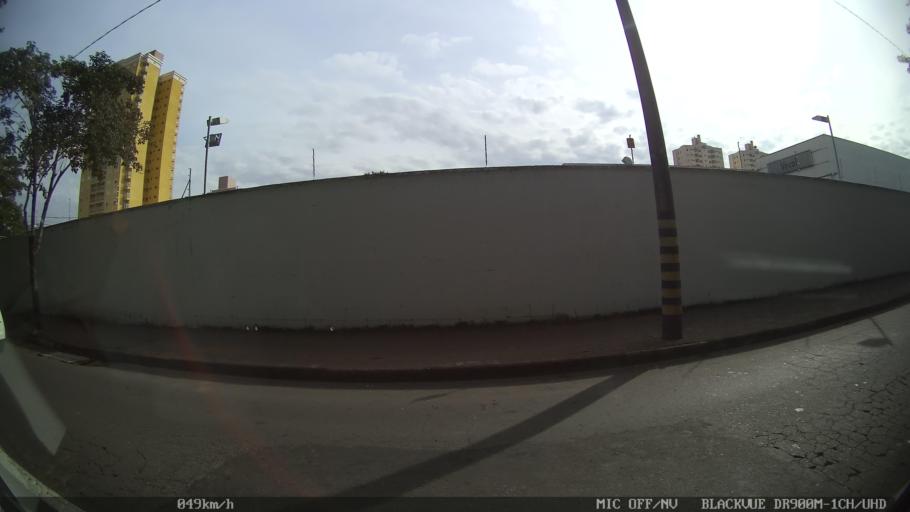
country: BR
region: Sao Paulo
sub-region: Piracicaba
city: Piracicaba
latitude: -22.7221
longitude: -47.6251
